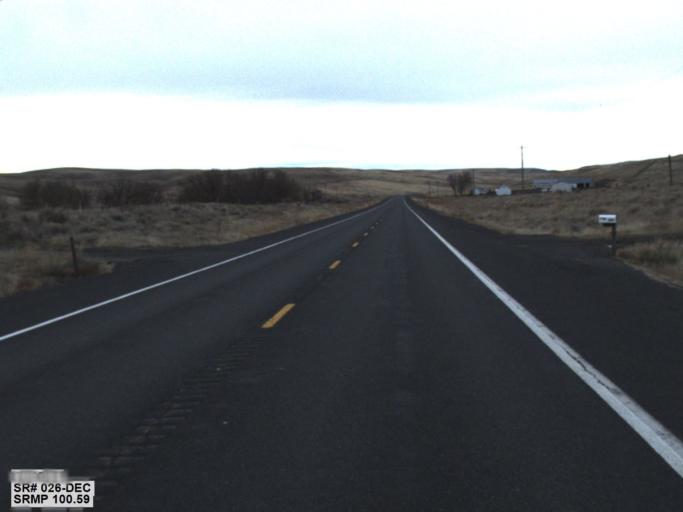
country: US
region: Washington
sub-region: Columbia County
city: Dayton
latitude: 46.7678
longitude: -117.9723
